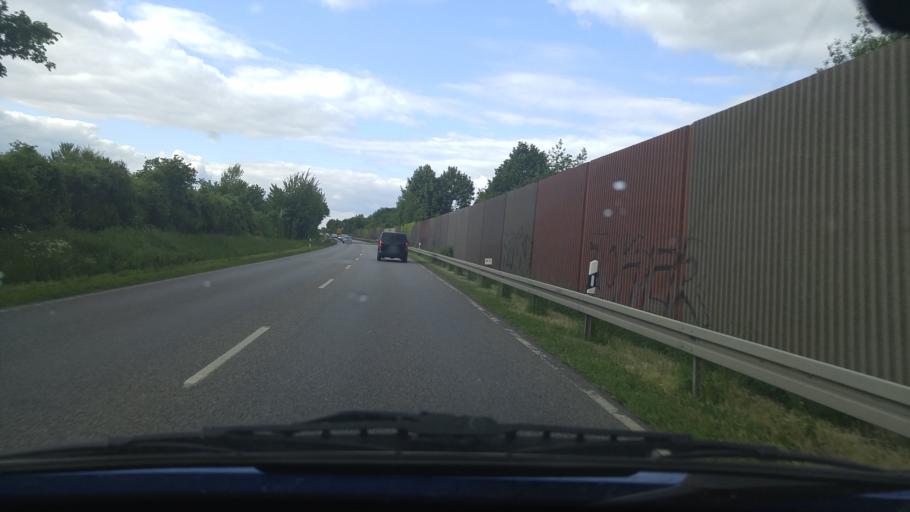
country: DE
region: Hesse
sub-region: Regierungsbezirk Darmstadt
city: Bad Vilbel
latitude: 50.2034
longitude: 8.7365
